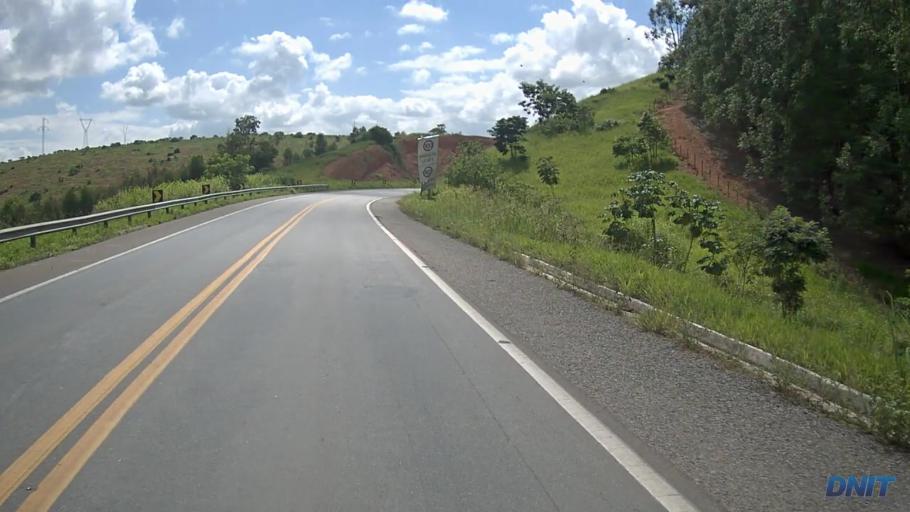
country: BR
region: Minas Gerais
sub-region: Governador Valadares
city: Governador Valadares
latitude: -19.0666
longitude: -42.1712
